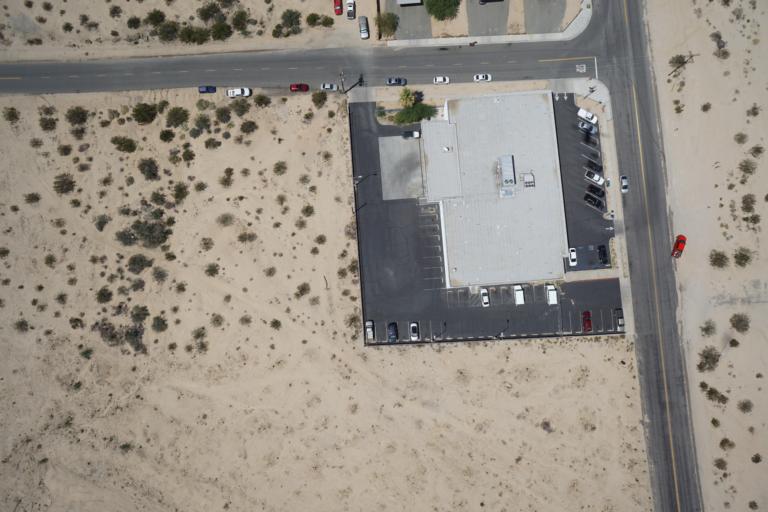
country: US
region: California
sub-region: San Bernardino County
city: Twentynine Palms
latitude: 34.1387
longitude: -116.0508
